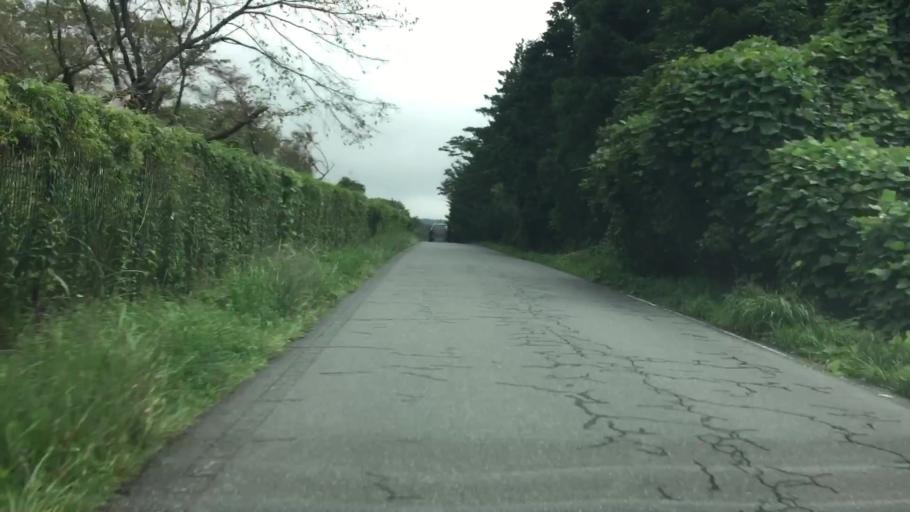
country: JP
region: Shizuoka
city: Fujinomiya
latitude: 35.3698
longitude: 138.5814
